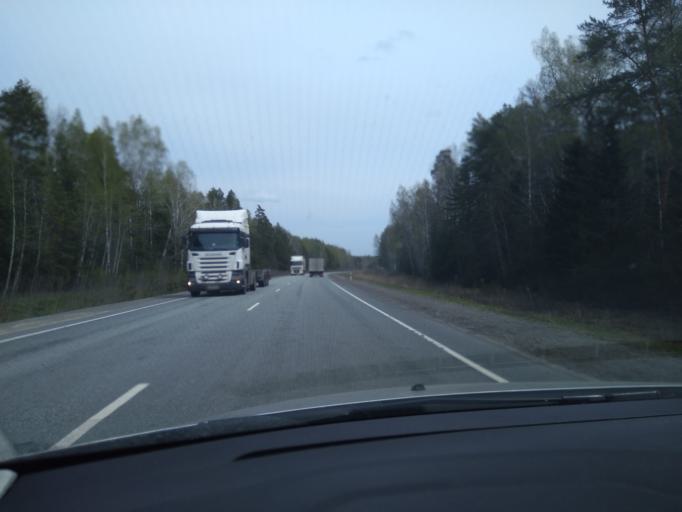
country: RU
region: Sverdlovsk
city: Yushala
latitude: 57.1126
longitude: 64.2341
